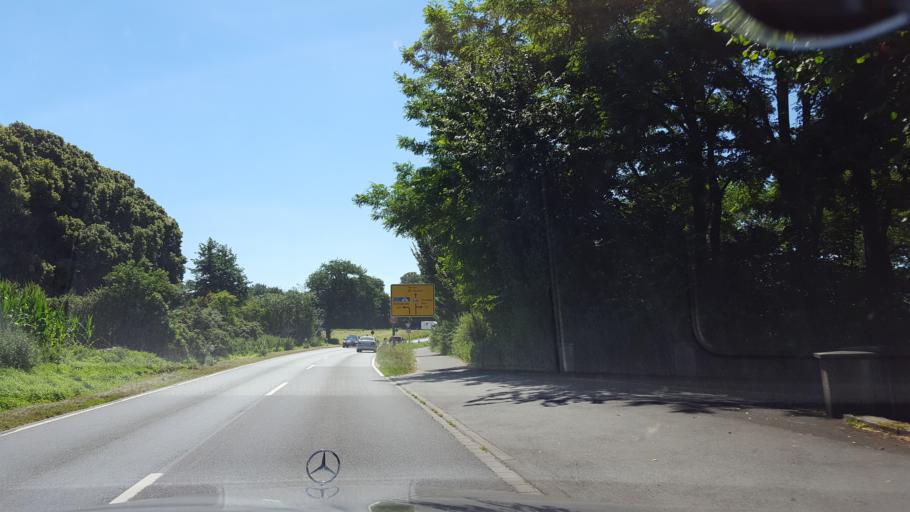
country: DE
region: North Rhine-Westphalia
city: Herten
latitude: 51.6287
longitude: 7.1581
